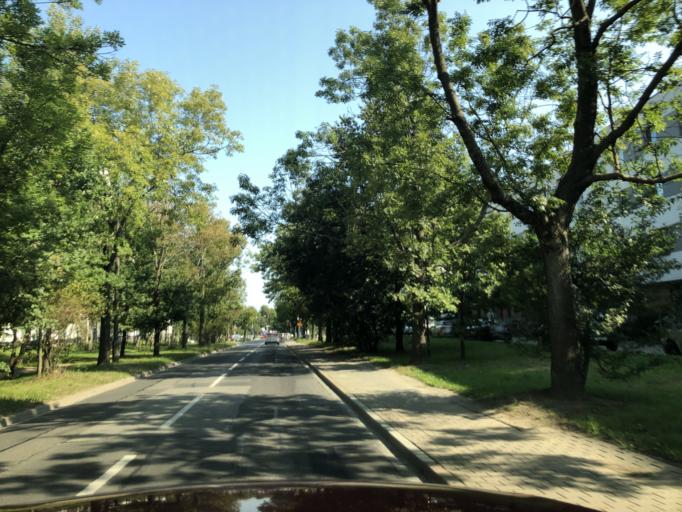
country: PL
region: Lower Silesian Voivodeship
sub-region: Powiat wroclawski
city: Smolec
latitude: 51.1621
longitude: 16.8951
